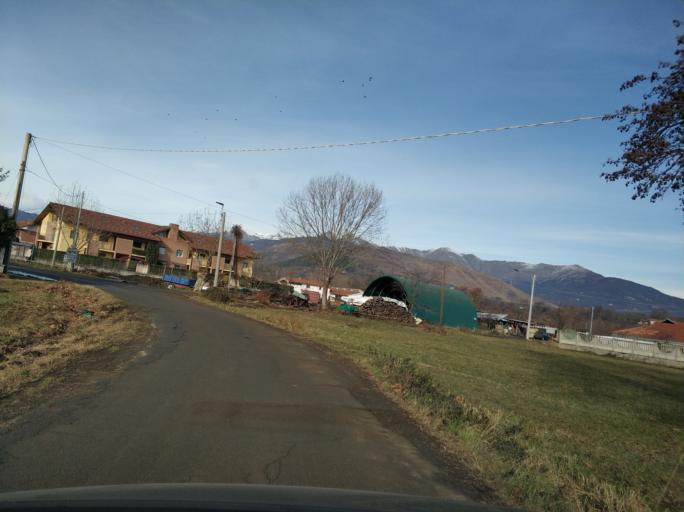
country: IT
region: Piedmont
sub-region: Provincia di Torino
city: Mathi
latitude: 45.2590
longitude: 7.5493
